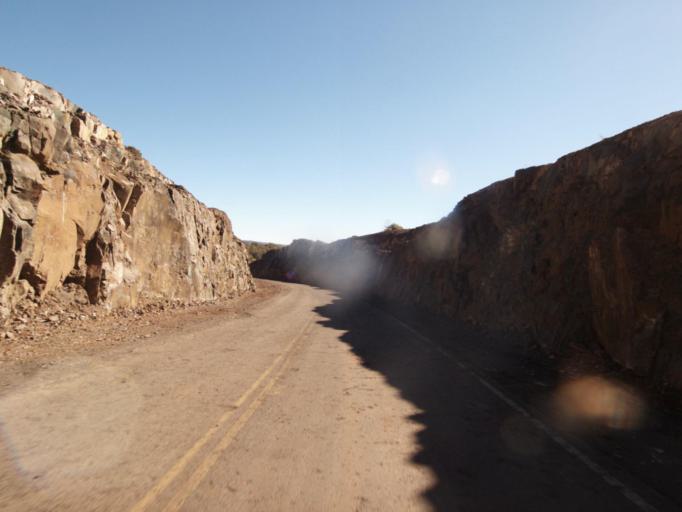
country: AR
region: Misiones
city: Bernardo de Irigoyen
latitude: -26.6130
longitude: -53.7181
